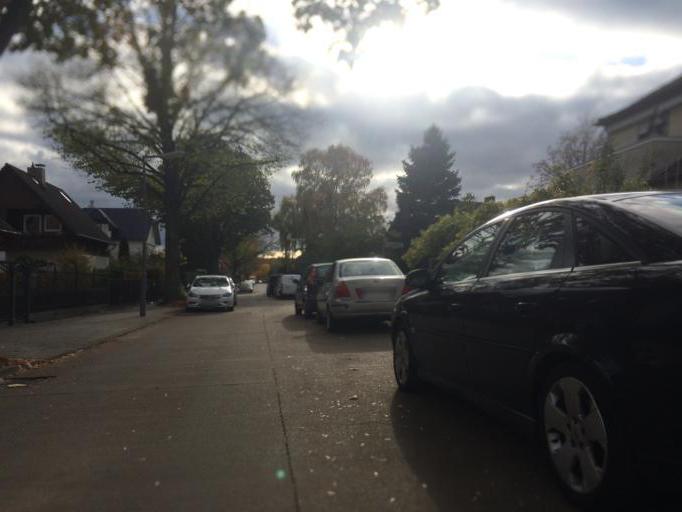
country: DE
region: Berlin
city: Markisches Viertel
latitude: 52.5946
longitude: 13.3563
